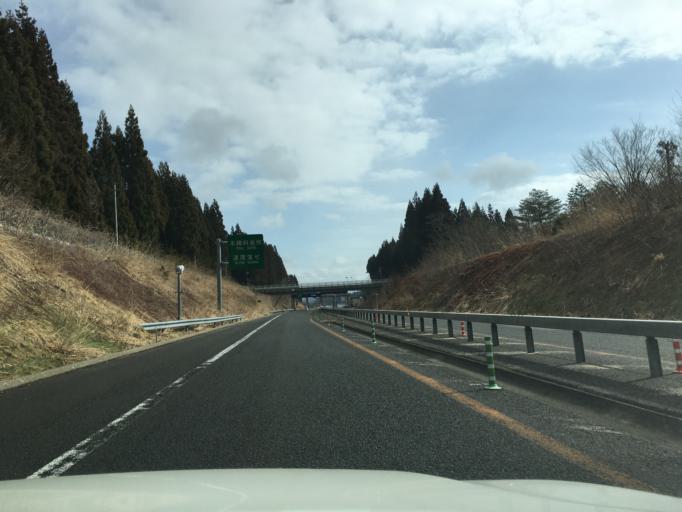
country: JP
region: Akita
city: Akita
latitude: 39.6346
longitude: 140.1760
